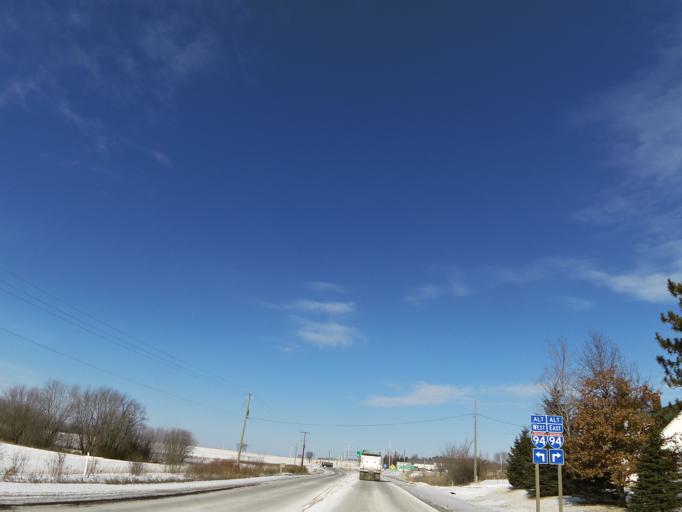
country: US
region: Wisconsin
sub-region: Saint Croix County
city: Roberts
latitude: 44.9896
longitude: -92.5580
